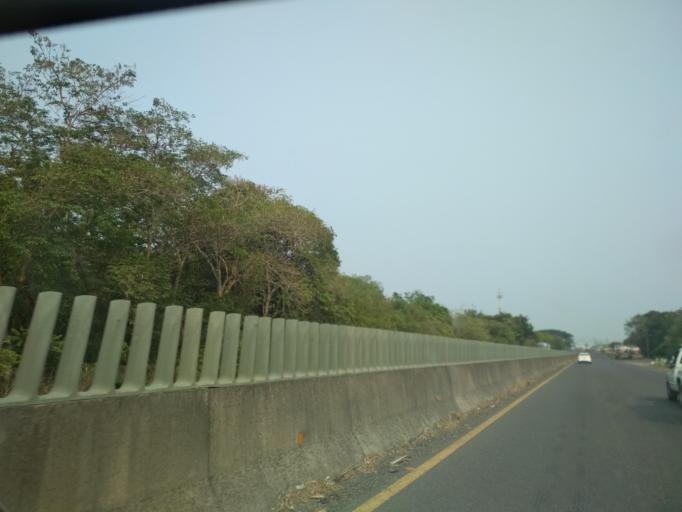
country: MX
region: Veracruz
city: El Tejar
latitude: 19.0899
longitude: -96.2039
